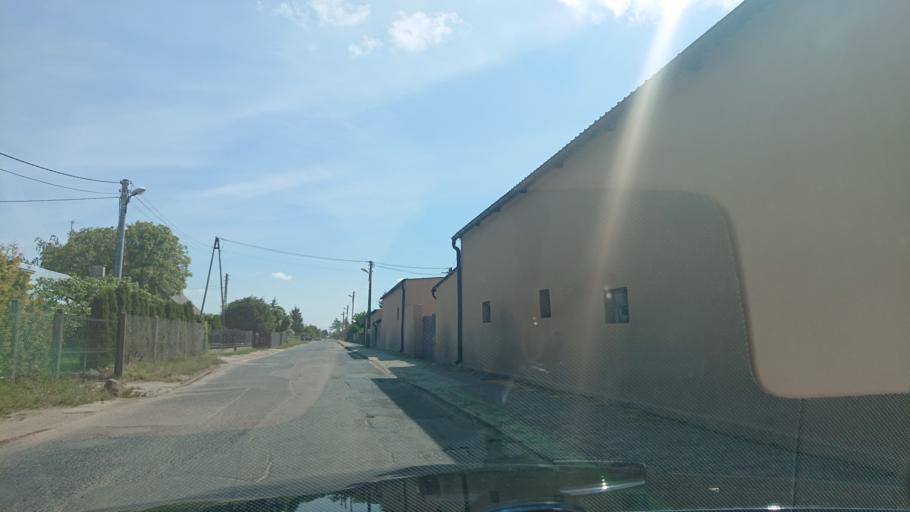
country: PL
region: Greater Poland Voivodeship
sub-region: Powiat gnieznienski
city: Gniezno
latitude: 52.4538
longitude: 17.5910
